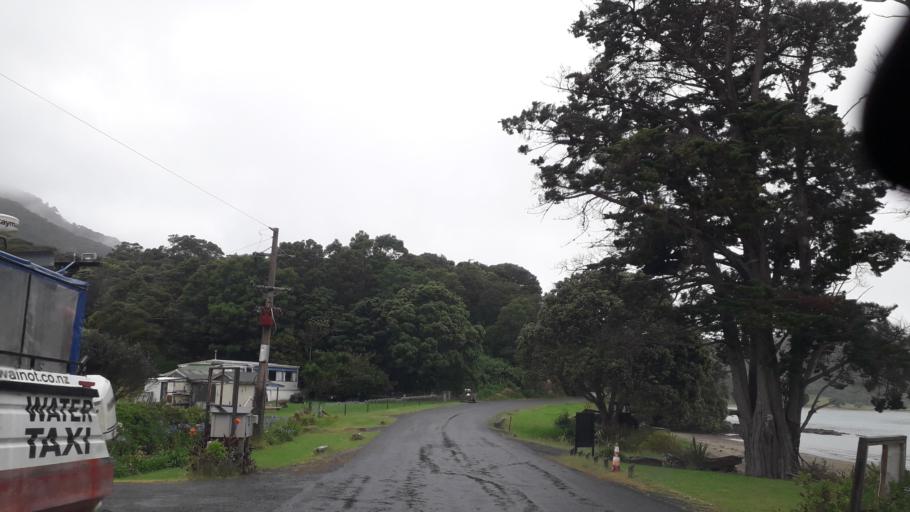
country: NZ
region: Northland
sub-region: Far North District
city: Paihia
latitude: -35.2318
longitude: 174.2608
